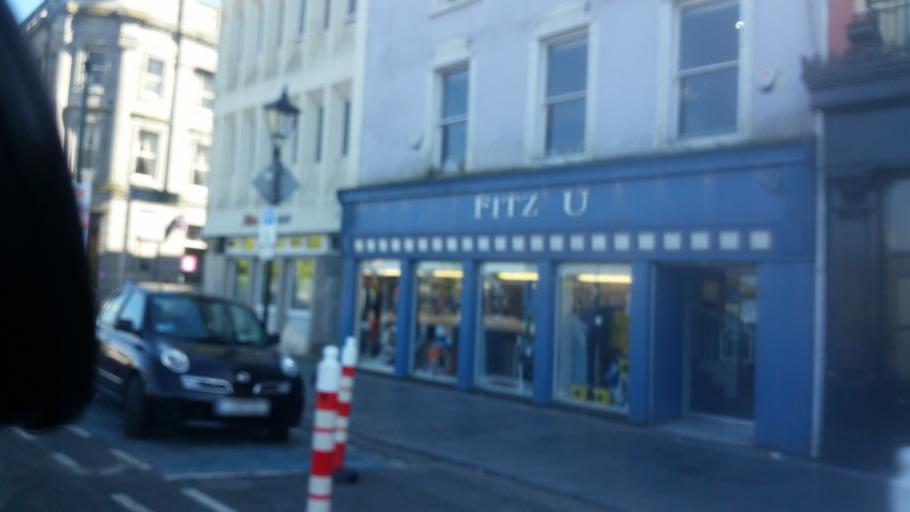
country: IE
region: Munster
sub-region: Waterford
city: Waterford
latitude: 52.2621
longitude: -7.1116
